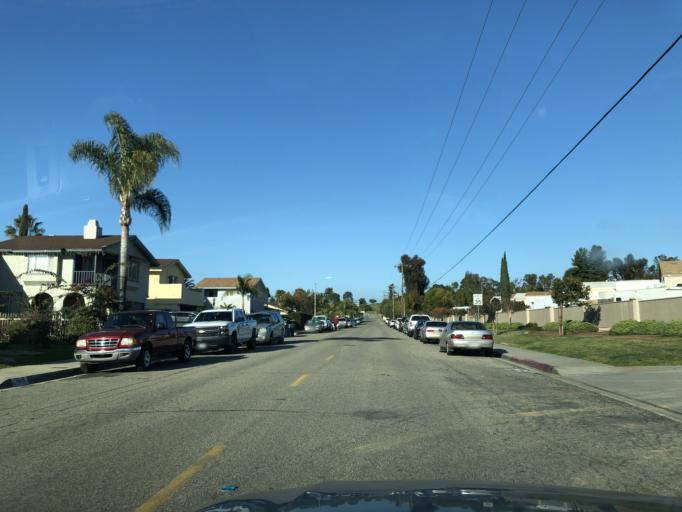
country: US
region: California
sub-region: San Diego County
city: Escondido
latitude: 33.1338
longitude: -117.1014
